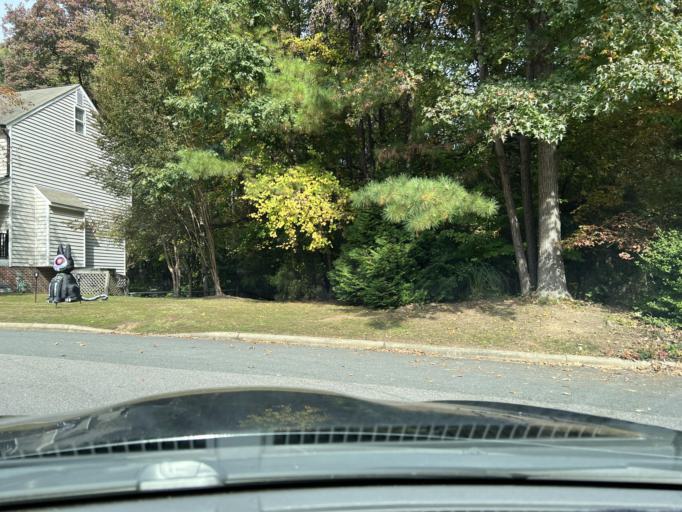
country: US
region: North Carolina
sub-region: Wake County
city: Wake Forest
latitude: 35.8960
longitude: -78.5870
